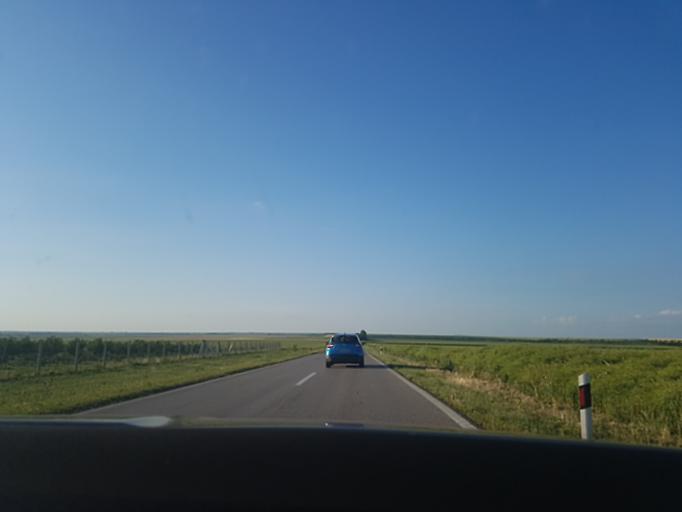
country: RS
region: Autonomna Pokrajina Vojvodina
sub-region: Juznobanatski Okrug
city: Vrsac
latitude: 45.1681
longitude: 21.2927
